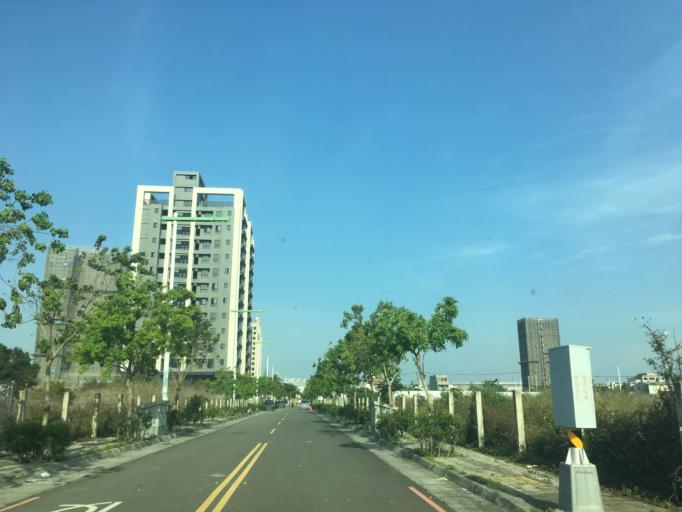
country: TW
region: Taiwan
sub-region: Taichung City
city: Taichung
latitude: 24.1938
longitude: 120.7094
